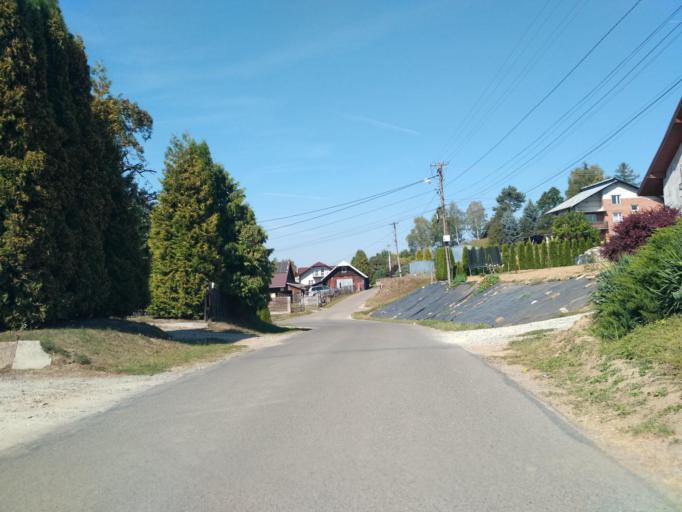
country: PL
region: Subcarpathian Voivodeship
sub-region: Powiat brzozowski
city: Grabownica Starzenska
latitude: 49.6506
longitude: 22.0867
